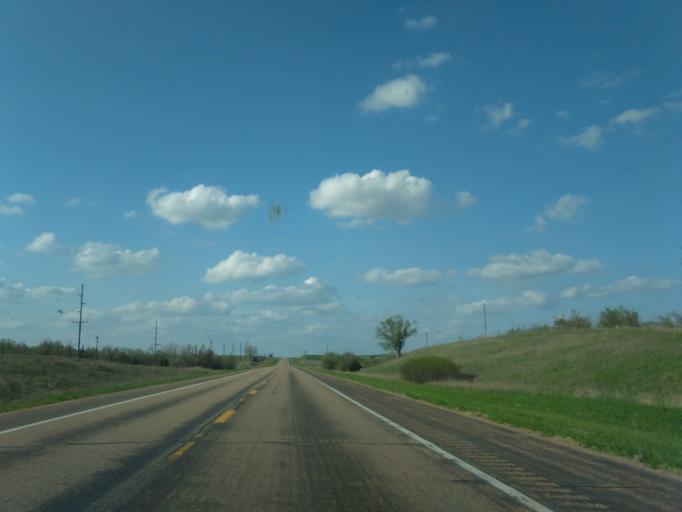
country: US
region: Nebraska
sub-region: Webster County
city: Red Cloud
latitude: 40.1115
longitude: -98.5188
